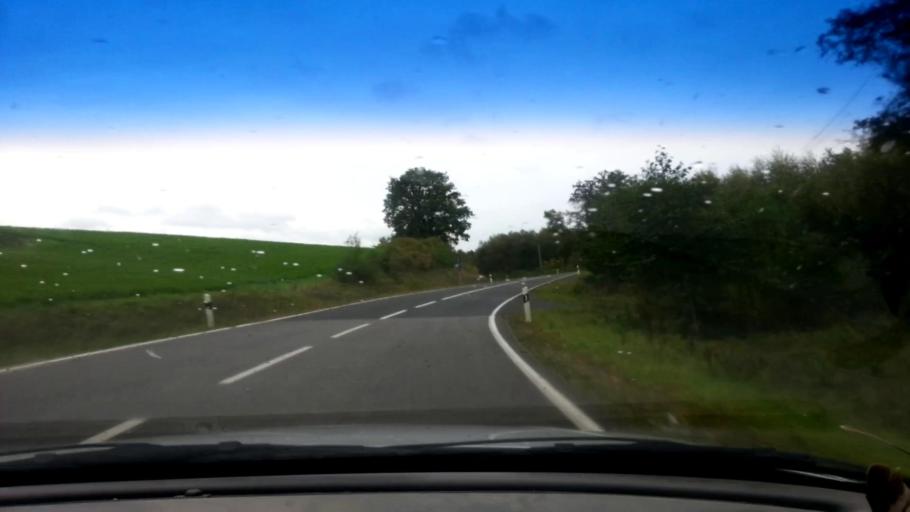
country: DE
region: Bavaria
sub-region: Regierungsbezirk Unterfranken
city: Stettfeld
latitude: 49.9949
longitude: 10.7514
